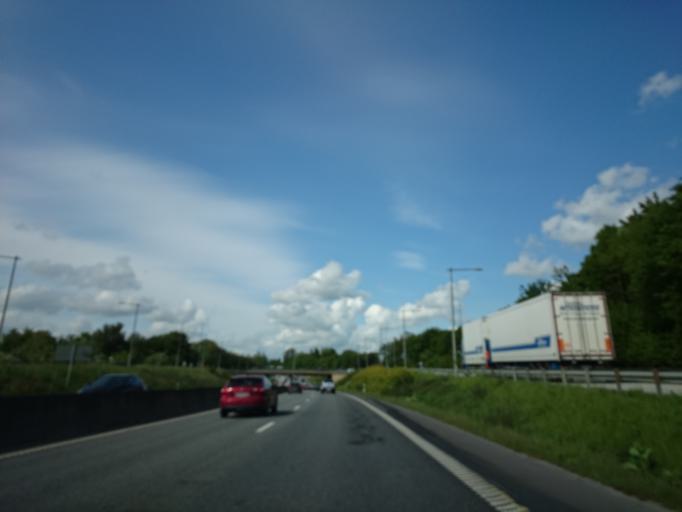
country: SE
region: Skane
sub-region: Lunds Kommun
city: Lund
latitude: 55.6968
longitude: 13.2164
